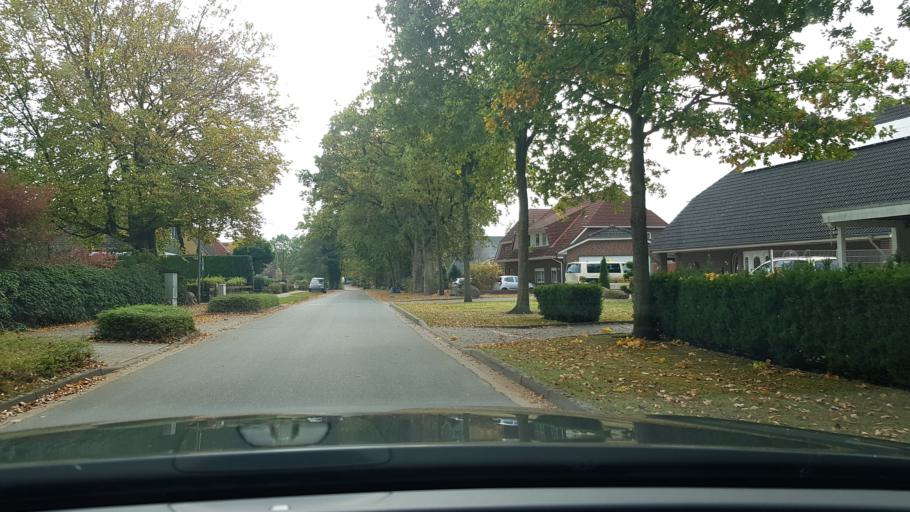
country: DE
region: Lower Saxony
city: Beverstedt
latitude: 53.4297
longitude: 8.8132
